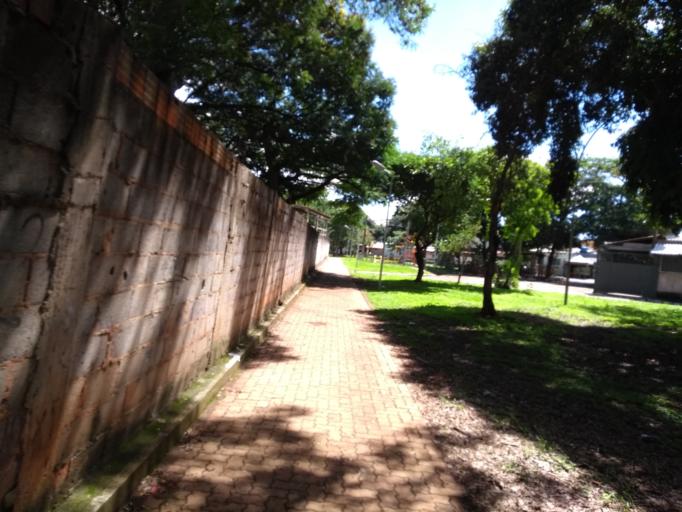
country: BR
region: Federal District
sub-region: Brasilia
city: Brasilia
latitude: -15.7872
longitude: -47.9388
